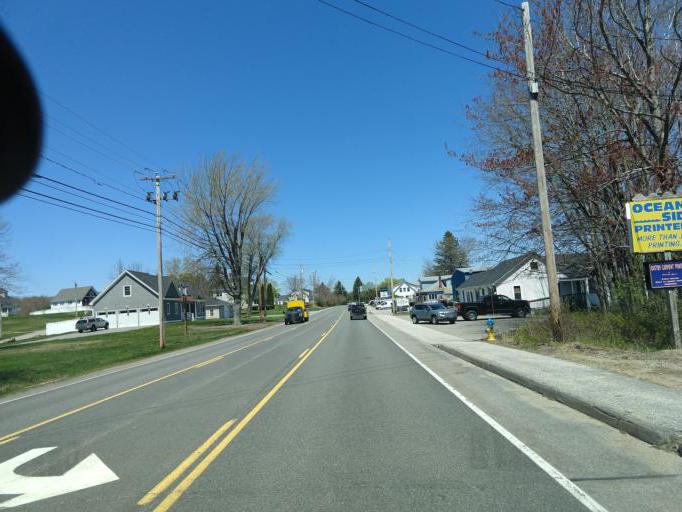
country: US
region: Maine
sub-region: York County
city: Wells Beach Station
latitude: 43.3112
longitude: -70.5847
